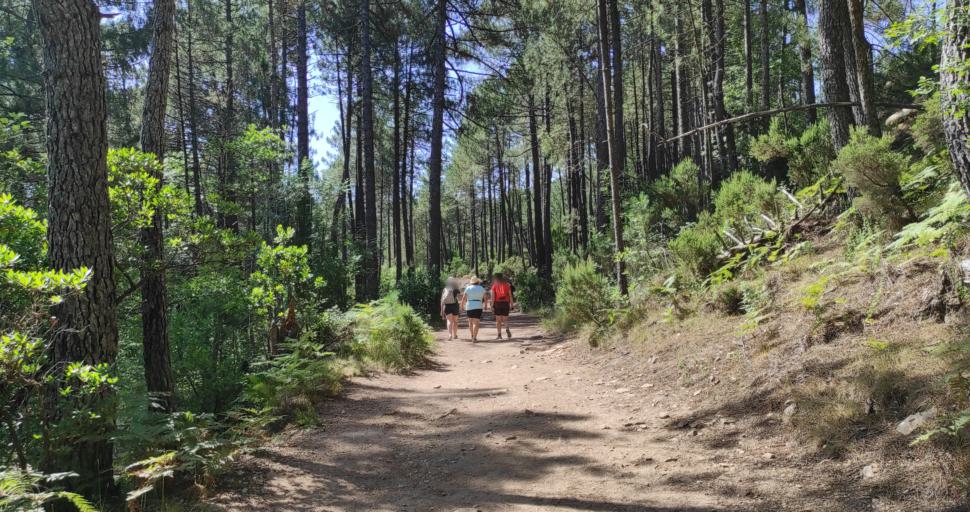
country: FR
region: Corsica
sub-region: Departement de la Corse-du-Sud
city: Zonza
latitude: 41.6805
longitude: 9.2095
